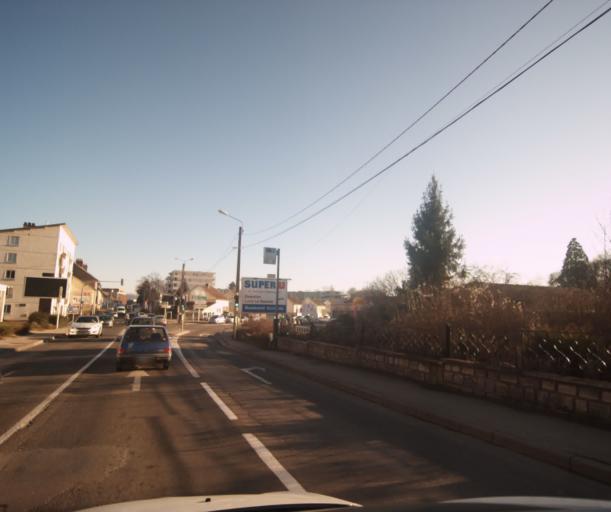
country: FR
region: Franche-Comte
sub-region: Departement du Doubs
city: Besancon
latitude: 47.2568
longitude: 6.0121
